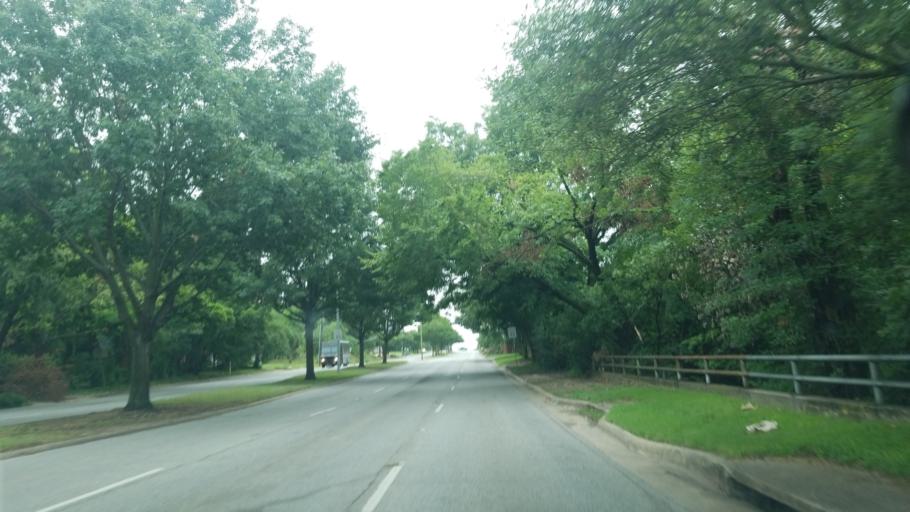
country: US
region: Texas
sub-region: Dallas County
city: Farmers Branch
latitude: 32.8871
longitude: -96.8563
